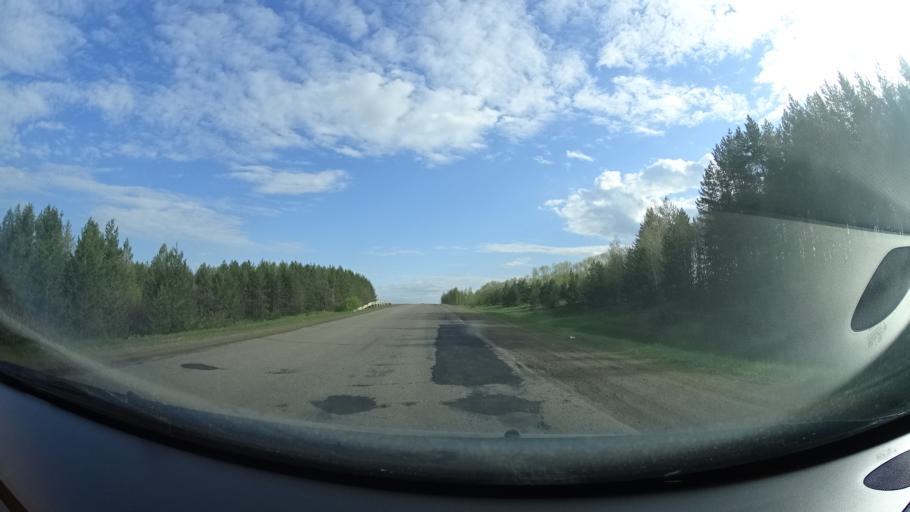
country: RU
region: Bashkortostan
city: Blagoveshchensk
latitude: 55.1396
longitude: 55.8471
